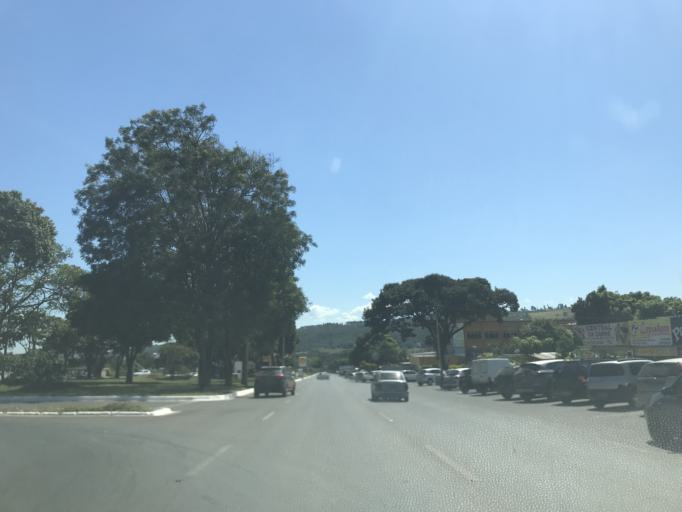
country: BR
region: Federal District
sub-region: Brasilia
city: Brasilia
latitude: -15.6482
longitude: -47.7855
